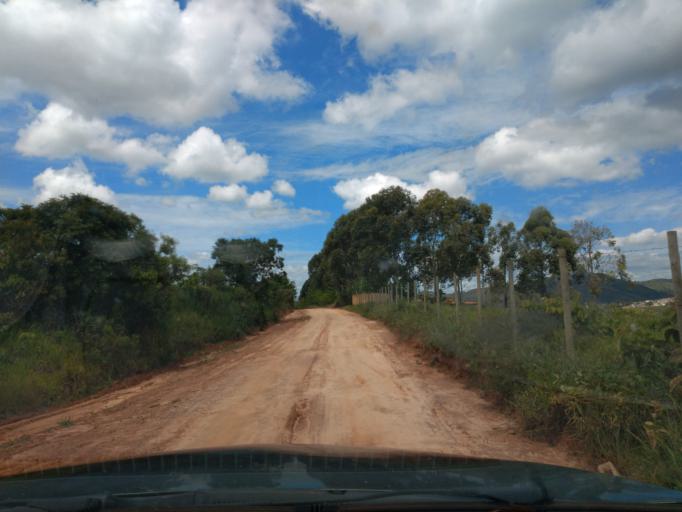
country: BR
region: Minas Gerais
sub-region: Lavras
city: Lavras
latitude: -21.5118
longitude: -44.9282
